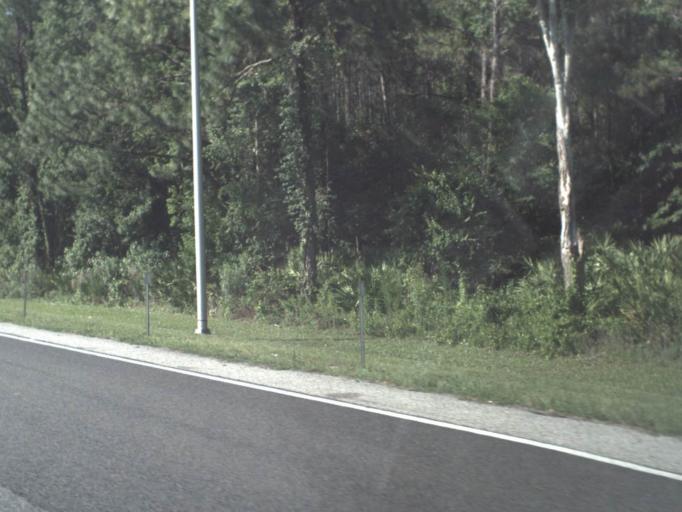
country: US
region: Florida
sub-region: Saint Johns County
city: Saint Augustine Shores
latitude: 29.7072
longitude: -81.3301
